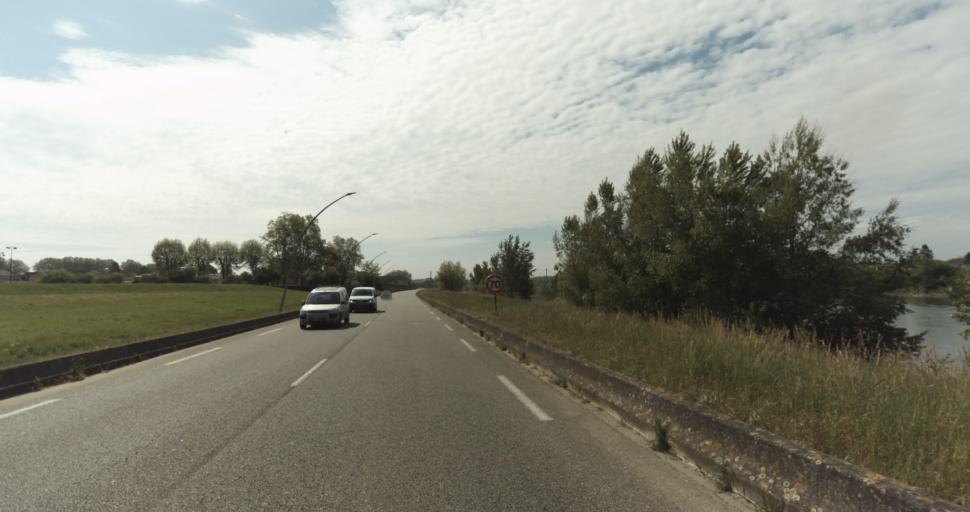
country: FR
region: Aquitaine
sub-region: Departement du Lot-et-Garonne
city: Le Passage
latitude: 44.2080
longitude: 0.6070
